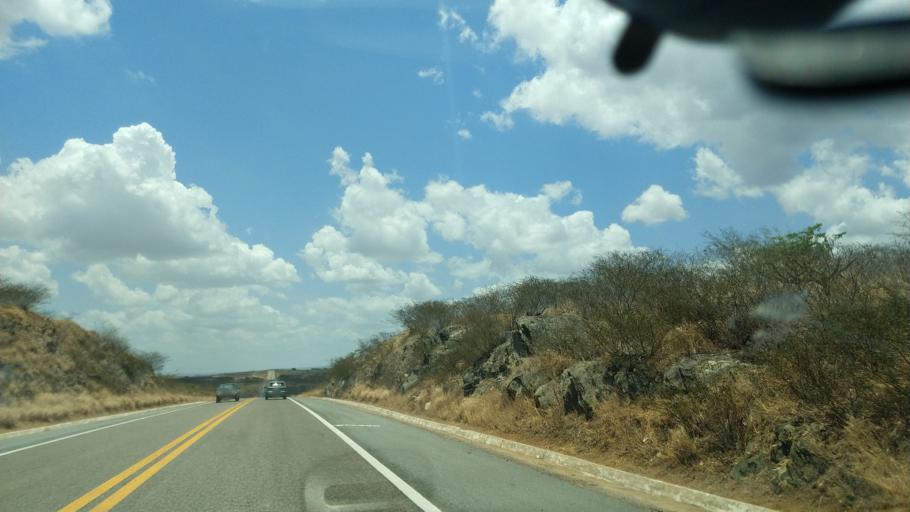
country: BR
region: Rio Grande do Norte
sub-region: Cerro Cora
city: Cerro Cora
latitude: -6.2046
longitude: -36.3252
